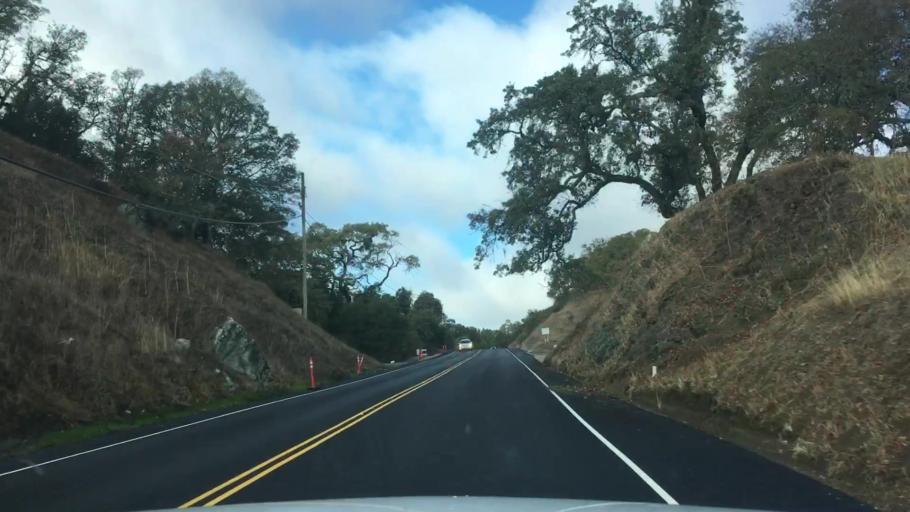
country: US
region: California
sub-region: San Luis Obispo County
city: Atascadero
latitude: 35.4521
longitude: -120.7088
